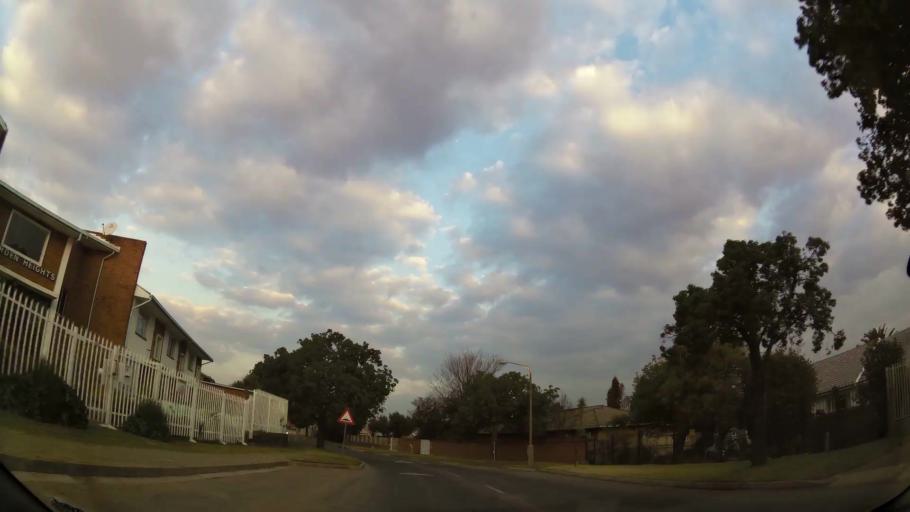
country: ZA
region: Gauteng
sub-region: Ekurhuleni Metropolitan Municipality
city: Benoni
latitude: -26.1757
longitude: 28.2996
